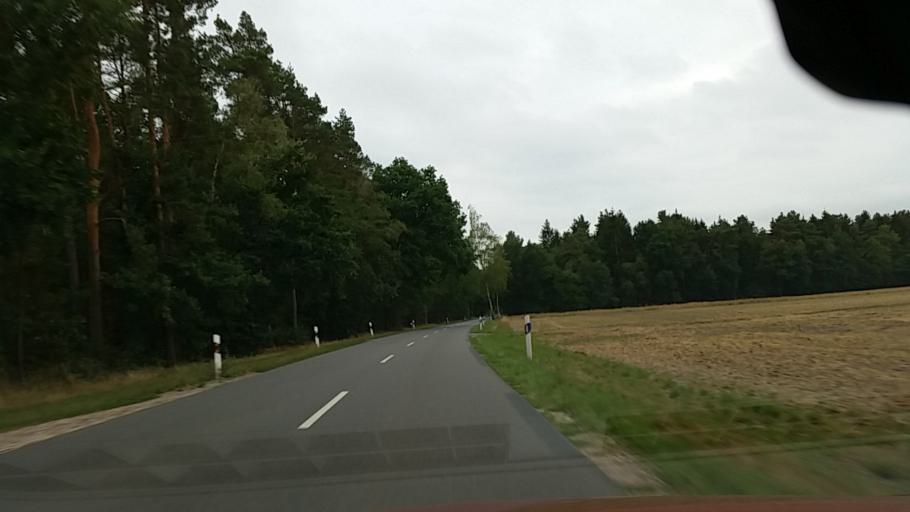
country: DE
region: Lower Saxony
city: Schoneworde
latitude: 52.6443
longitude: 10.6987
